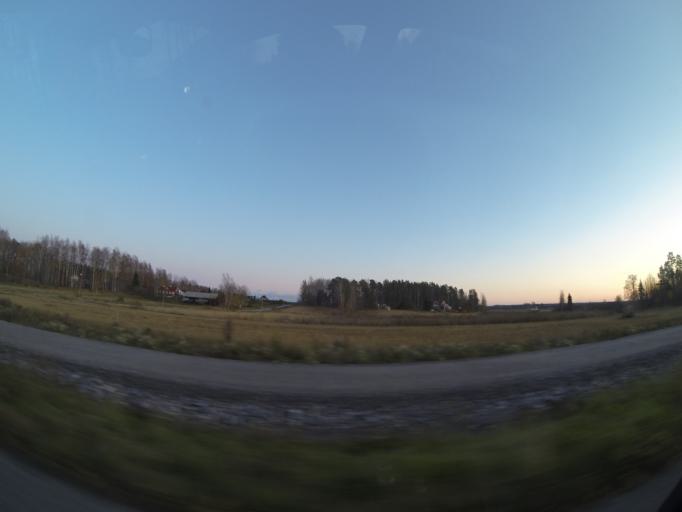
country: SE
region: OErebro
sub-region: Lindesbergs Kommun
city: Frovi
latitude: 59.3173
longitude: 15.3866
